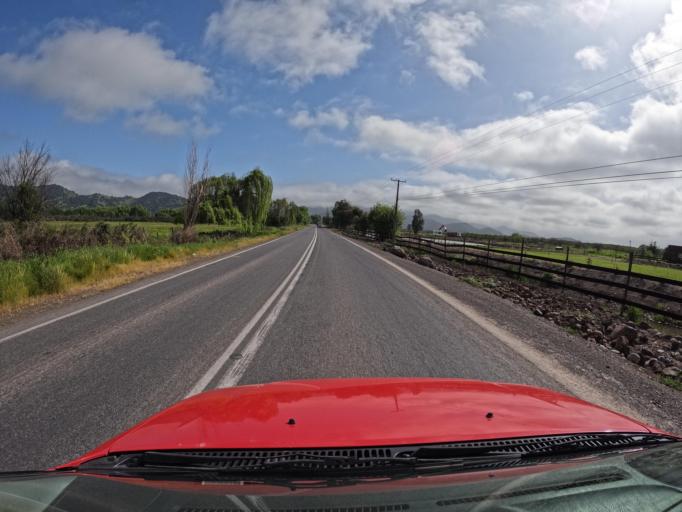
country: CL
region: Maule
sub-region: Provincia de Curico
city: Teno
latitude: -34.8445
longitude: -71.1864
